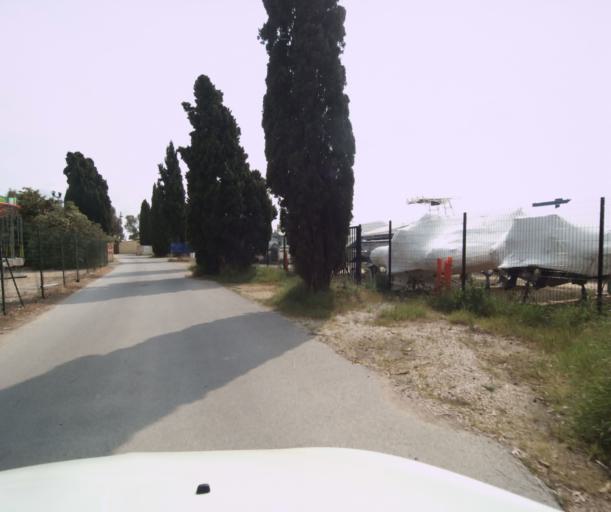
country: FR
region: Provence-Alpes-Cote d'Azur
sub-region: Departement du Var
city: Hyeres
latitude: 43.0867
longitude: 6.1453
